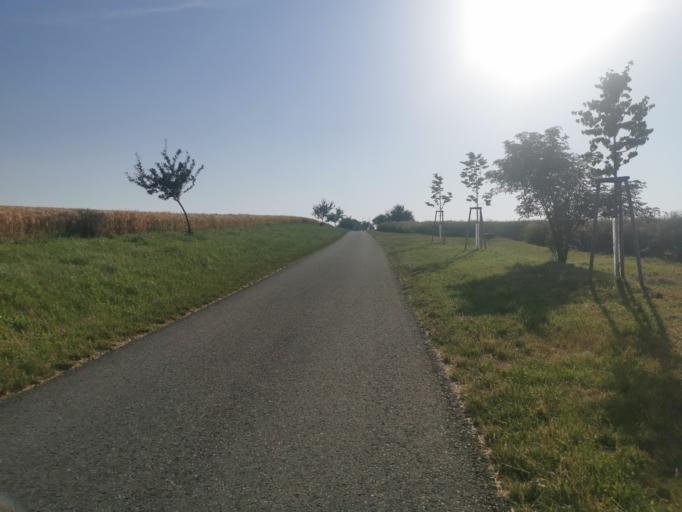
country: CZ
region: South Moravian
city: Vacenovice
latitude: 48.9429
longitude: 17.1653
